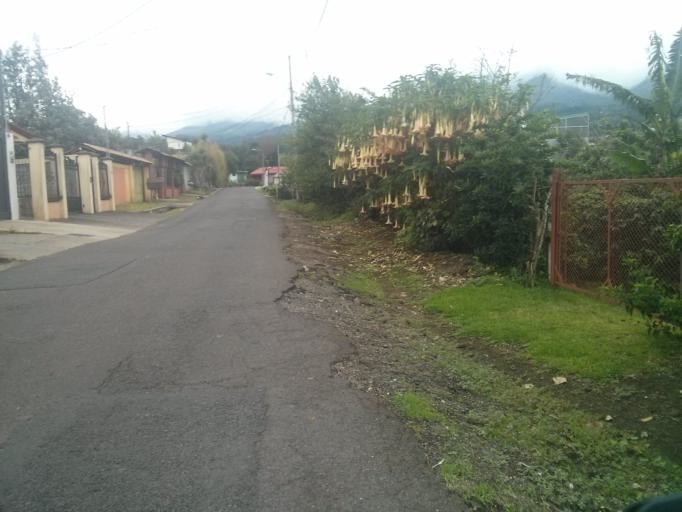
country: CR
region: Heredia
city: Angeles
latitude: 10.0202
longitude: -84.0490
